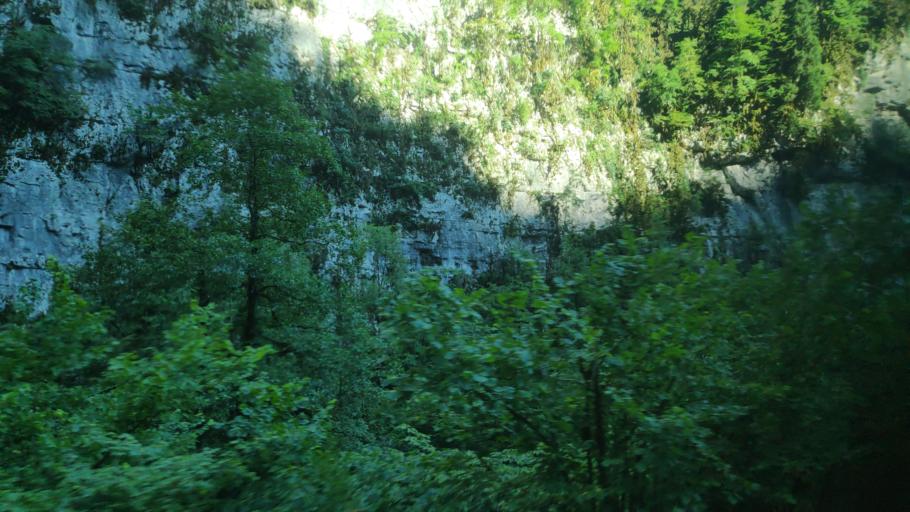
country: GE
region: Abkhazia
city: Gagra
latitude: 43.4355
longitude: 40.5316
